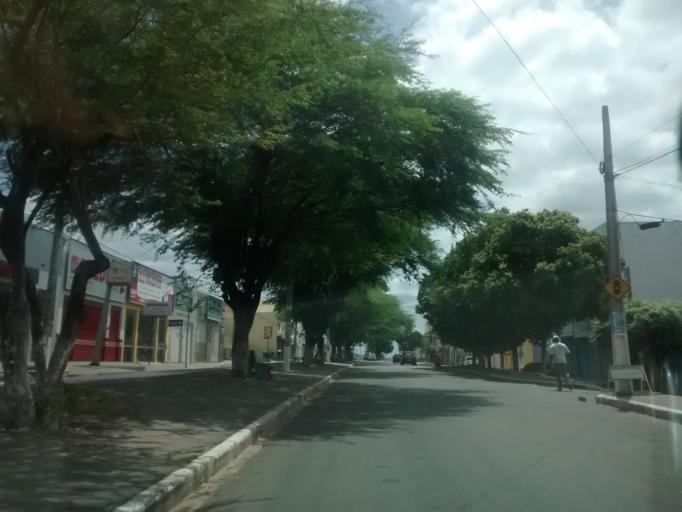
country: BR
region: Bahia
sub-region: Brumado
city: Brumado
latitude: -14.2119
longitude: -41.6738
